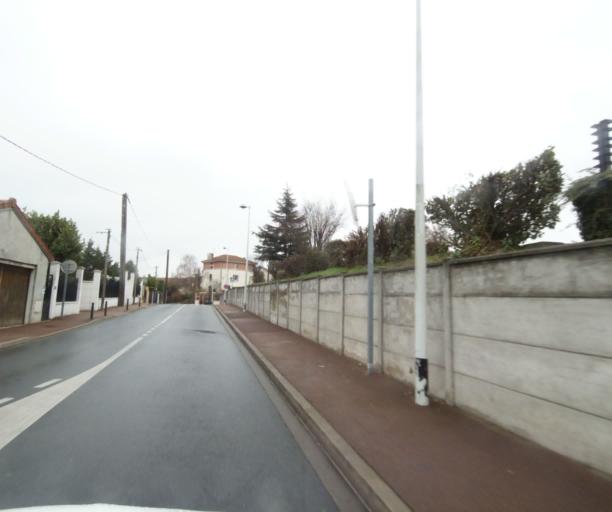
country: FR
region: Ile-de-France
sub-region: Departement des Hauts-de-Seine
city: Suresnes
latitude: 48.8798
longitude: 2.2164
